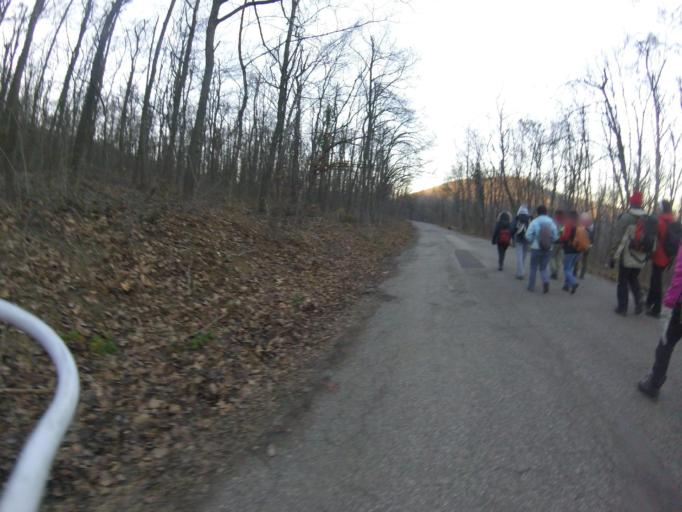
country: HU
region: Pest
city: Budakeszi
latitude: 47.5242
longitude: 18.9564
